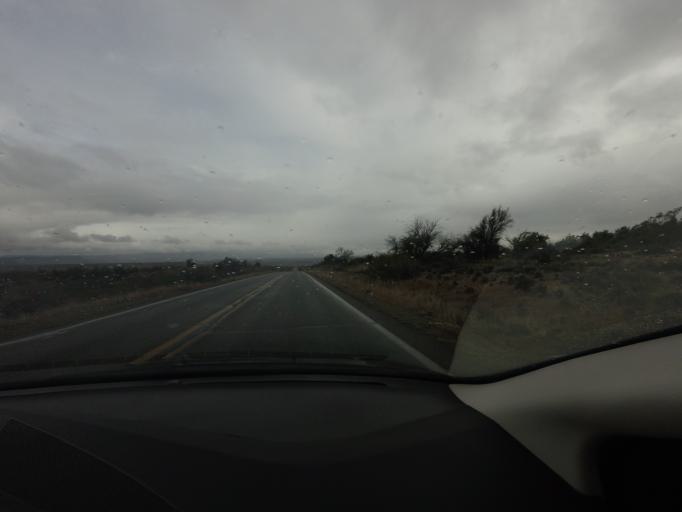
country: US
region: Arizona
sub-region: Yavapai County
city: Cornville
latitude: 34.6857
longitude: -111.8485
